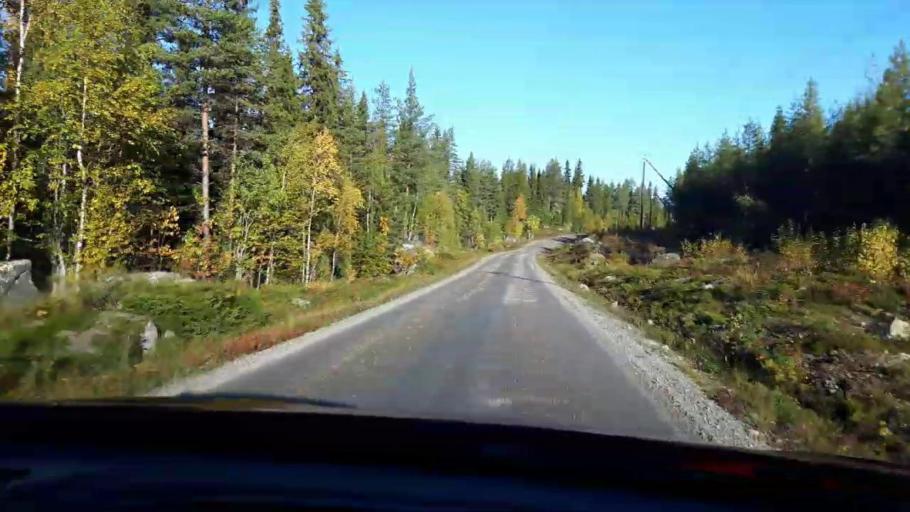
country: SE
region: Jaemtland
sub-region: Stroemsunds Kommun
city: Stroemsund
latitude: 64.3679
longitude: 15.1613
